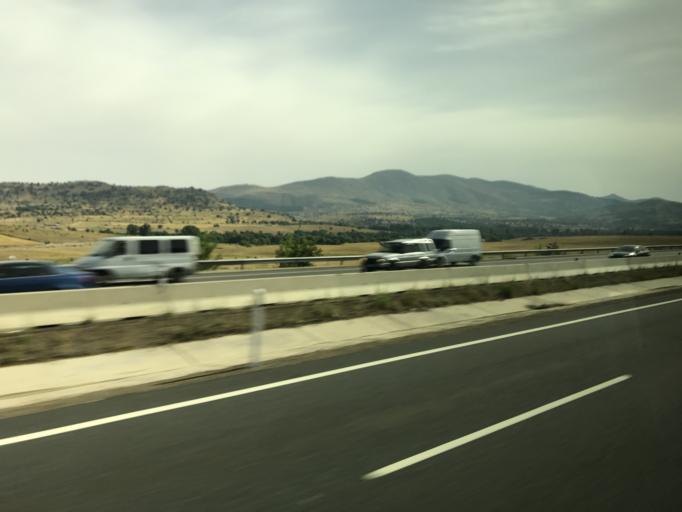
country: ES
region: Castille and Leon
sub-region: Provincia de Segovia
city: Vegas de Matute
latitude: 40.7385
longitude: -4.2313
